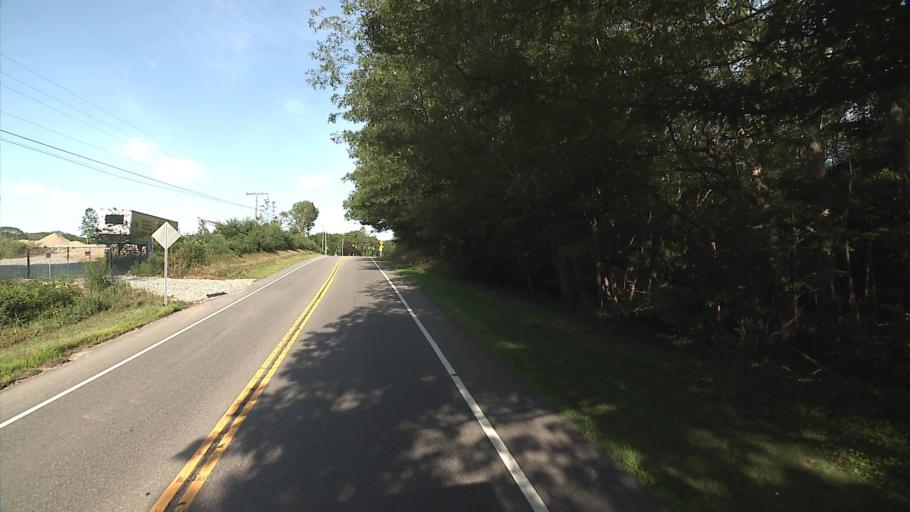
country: US
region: Connecticut
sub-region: New London County
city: Pawcatuck
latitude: 41.4378
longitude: -71.8775
